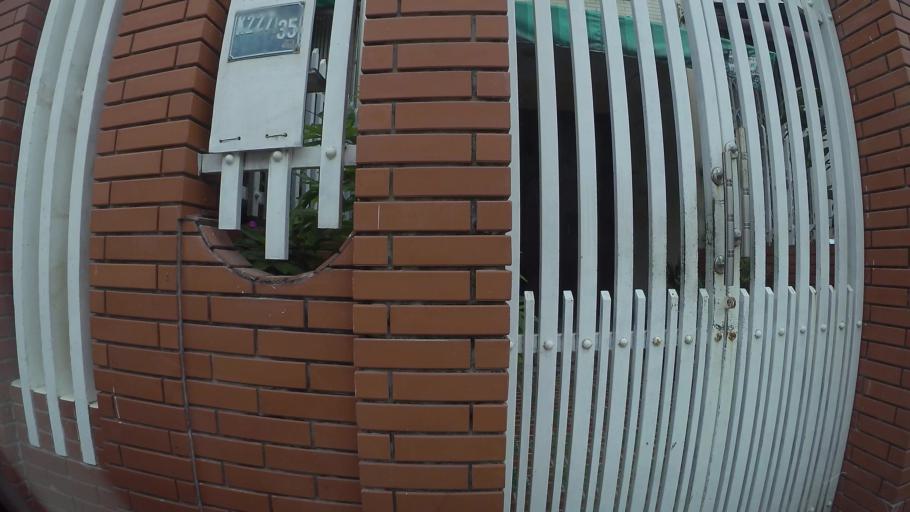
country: VN
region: Da Nang
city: Thanh Khe
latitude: 16.0519
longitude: 108.1828
